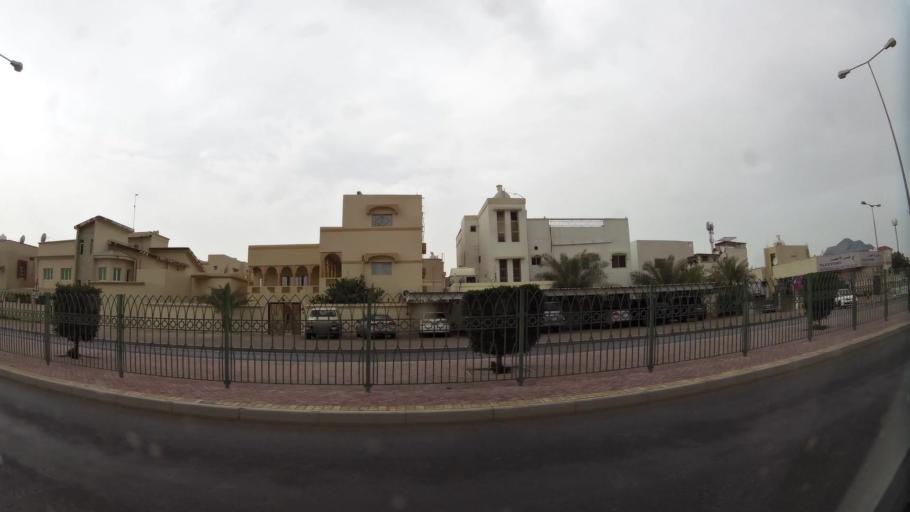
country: BH
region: Northern
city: Ar Rifa'
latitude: 26.1310
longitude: 50.5678
